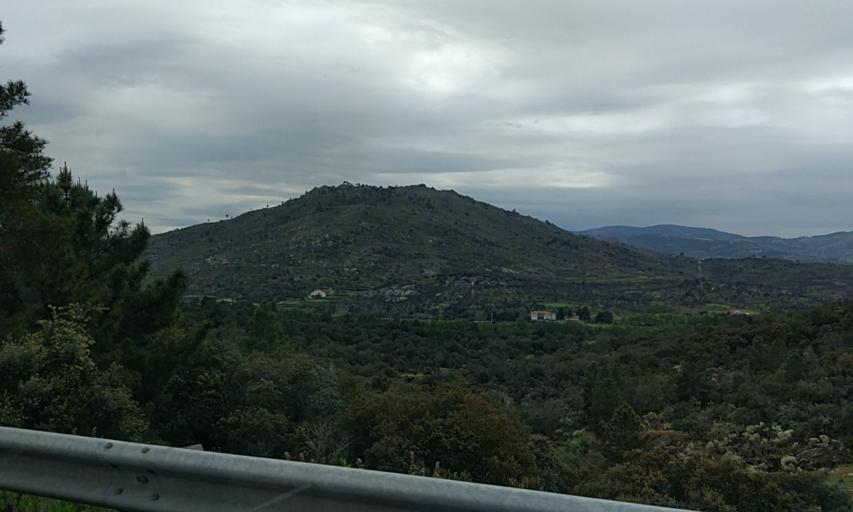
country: PT
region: Guarda
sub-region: Celorico da Beira
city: Celorico da Beira
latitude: 40.6291
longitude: -7.3087
